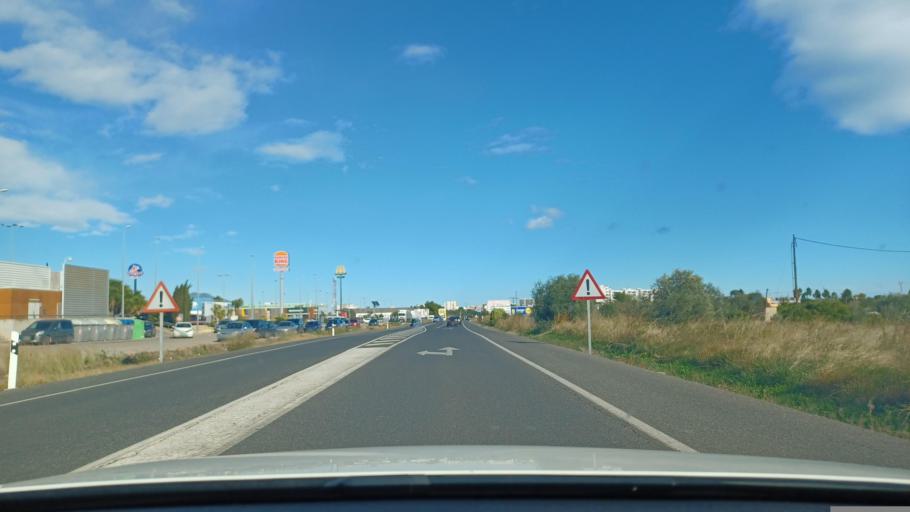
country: ES
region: Valencia
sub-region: Provincia de Castello
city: Vinaros
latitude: 40.4532
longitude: 0.4521
